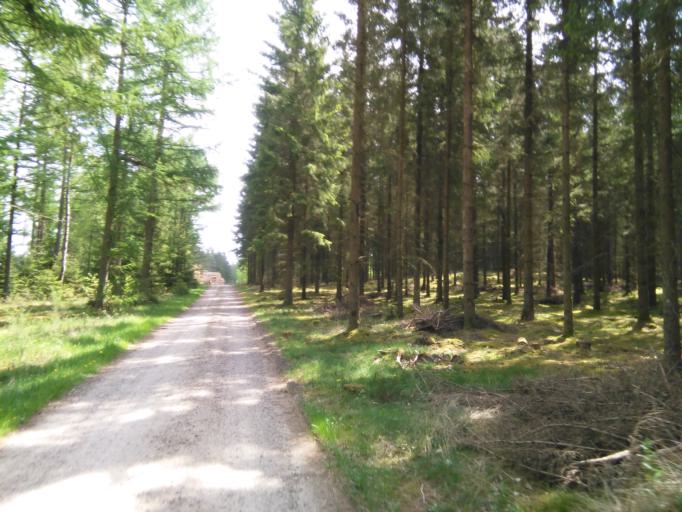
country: DK
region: Central Jutland
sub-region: Silkeborg Kommune
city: Svejbaek
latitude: 56.0579
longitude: 9.6522
